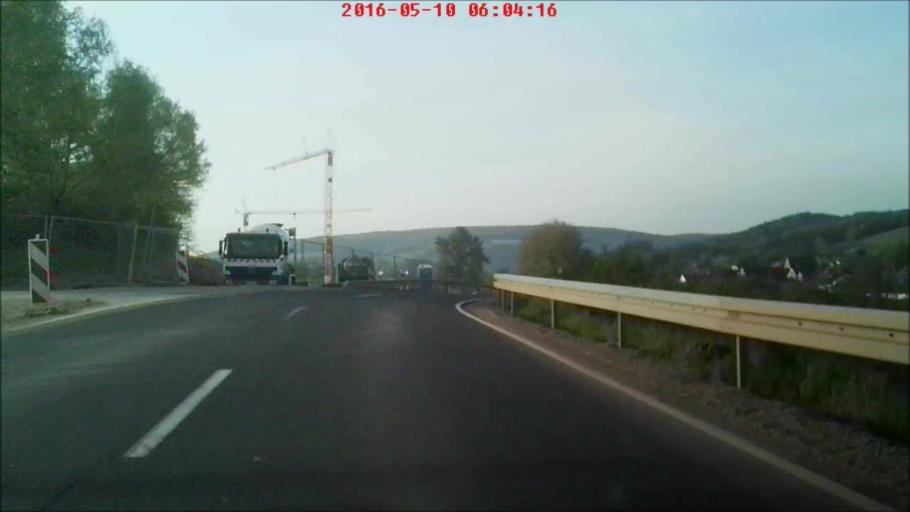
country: DE
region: Hesse
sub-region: Regierungsbezirk Kassel
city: Bad Hersfeld
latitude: 50.8311
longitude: 9.7257
